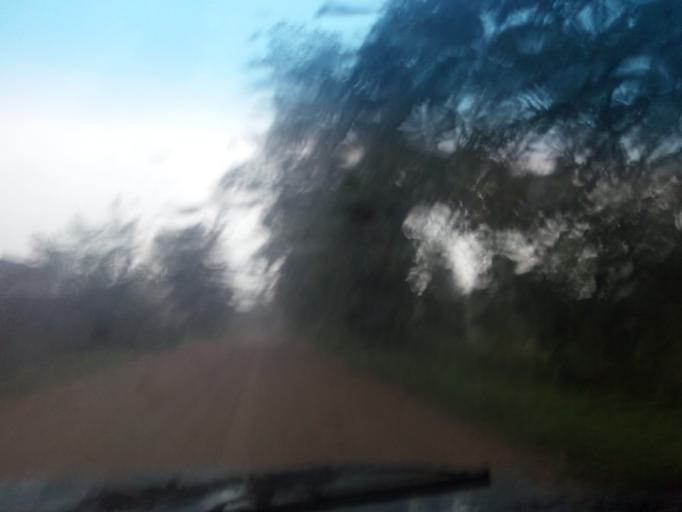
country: BY
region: Vitebsk
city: Dzisna
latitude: 55.6731
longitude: 28.3162
